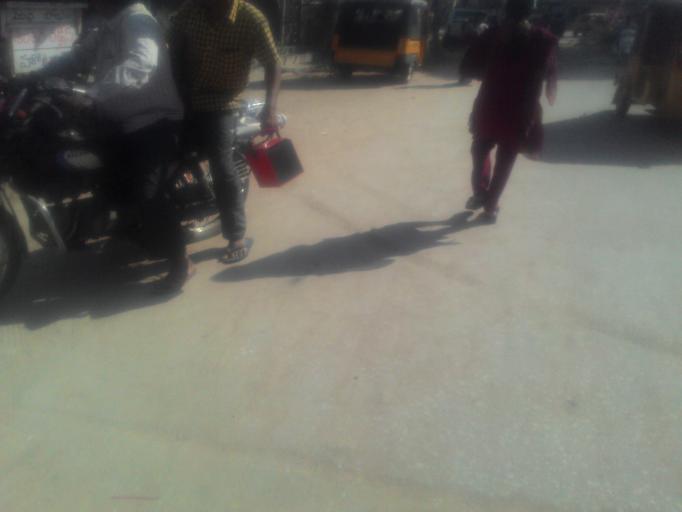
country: IN
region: Andhra Pradesh
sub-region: Chittoor
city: Madanapalle
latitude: 13.5584
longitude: 78.5087
